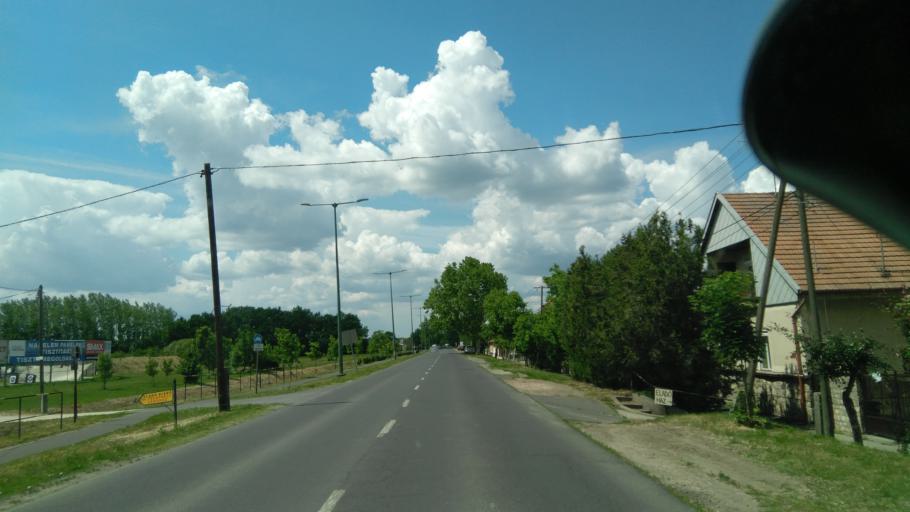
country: HU
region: Bekes
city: Gyula
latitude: 46.6490
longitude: 21.2498
